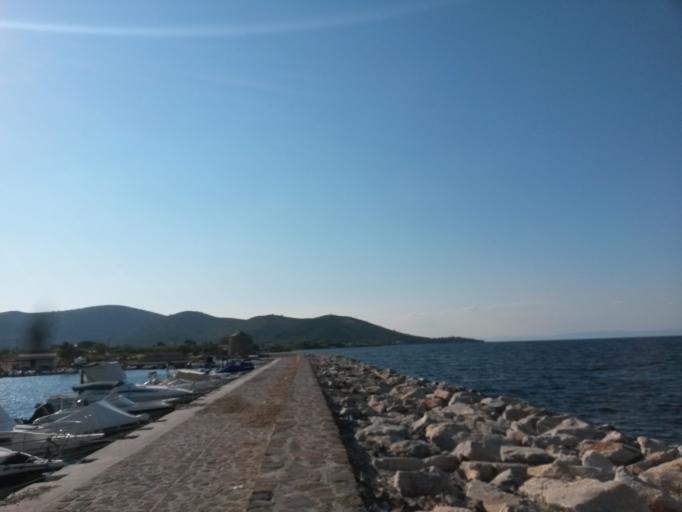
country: GR
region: North Aegean
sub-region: Nomos Lesvou
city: Pamfylla
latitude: 39.1818
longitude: 26.5004
